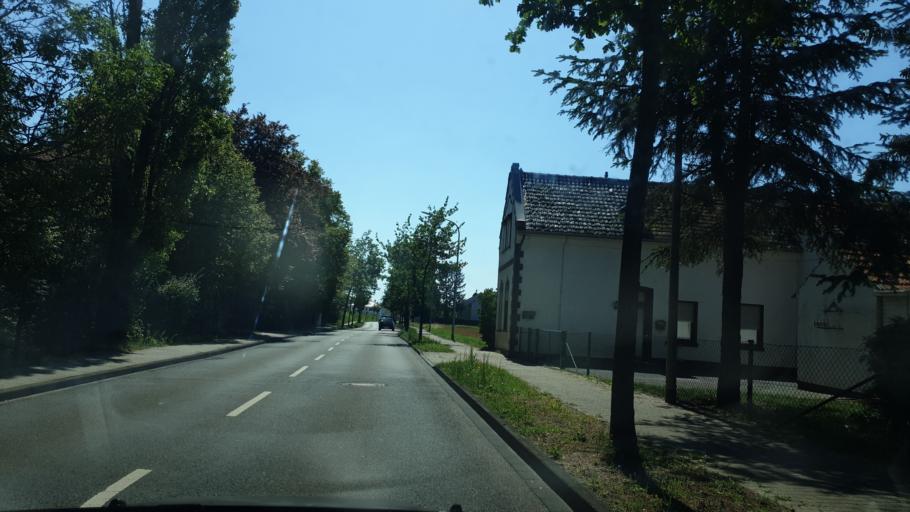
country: DE
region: North Rhine-Westphalia
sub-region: Regierungsbezirk Koln
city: Euskirchen
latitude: 50.6759
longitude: 6.7923
